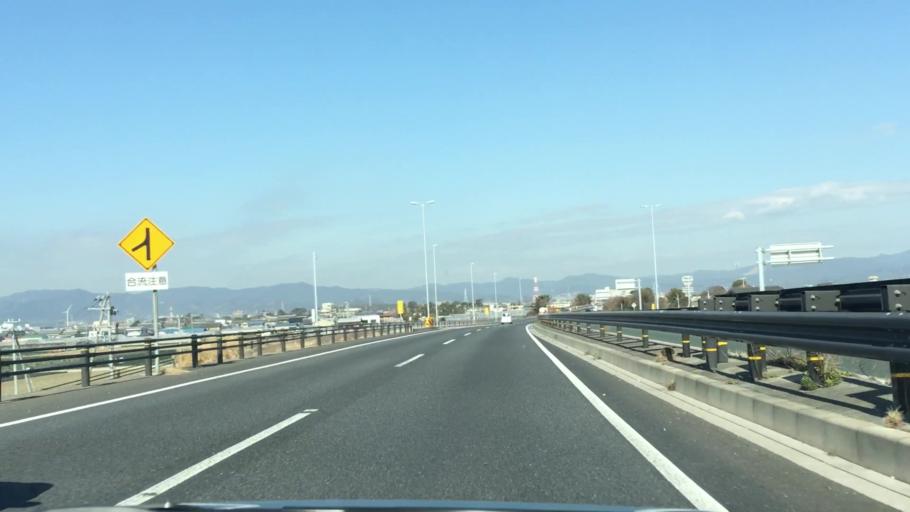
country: JP
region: Aichi
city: Kozakai-cho
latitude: 34.7627
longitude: 137.3325
